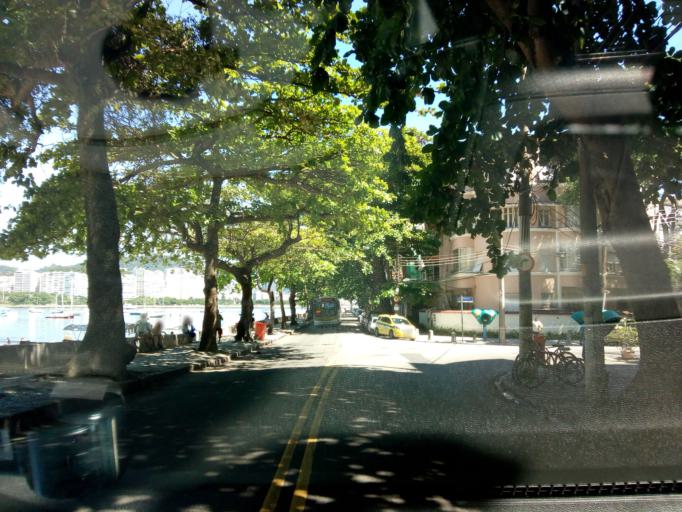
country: BR
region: Rio de Janeiro
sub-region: Rio De Janeiro
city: Rio de Janeiro
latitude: -22.9480
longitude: -43.1627
